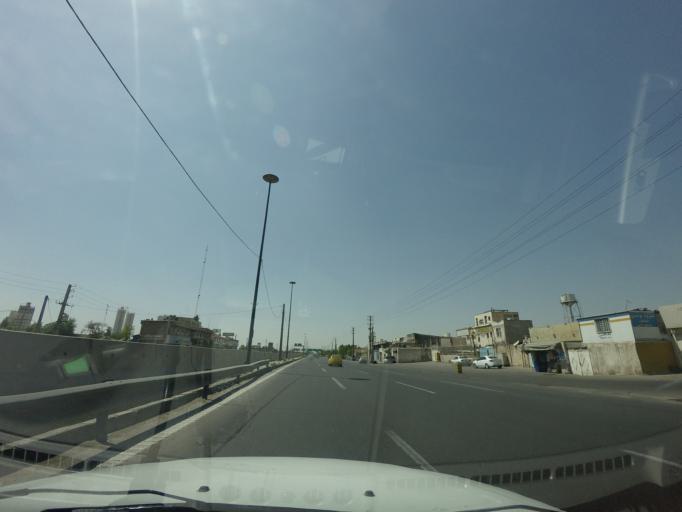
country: IR
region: Tehran
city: Rey
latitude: 35.6251
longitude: 51.3313
